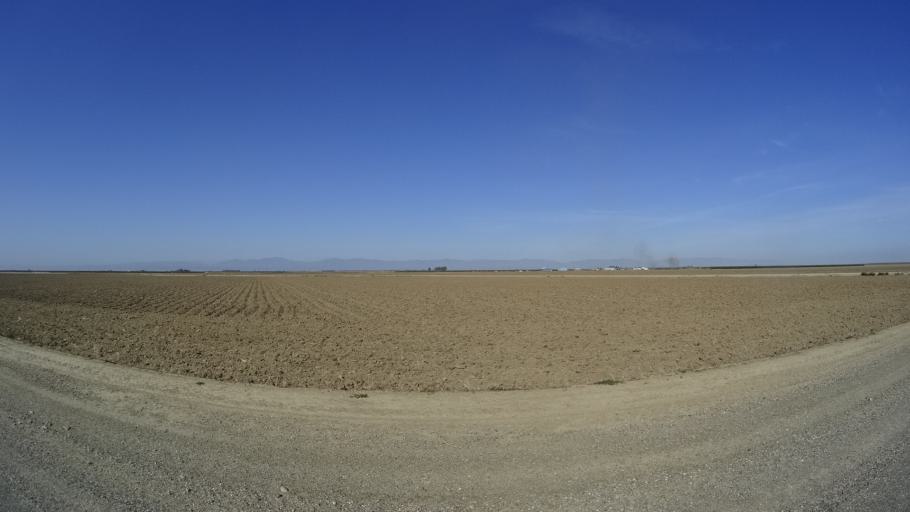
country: US
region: California
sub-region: Glenn County
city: Willows
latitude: 39.5981
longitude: -122.1169
